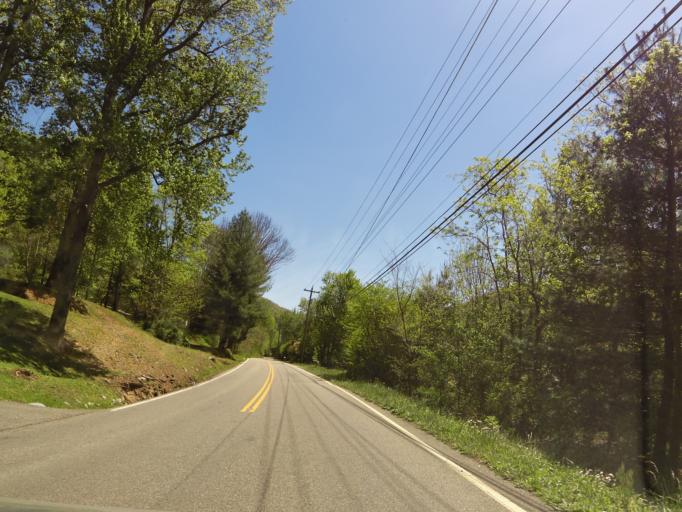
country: US
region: Tennessee
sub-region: Unicoi County
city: Erwin
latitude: 36.1658
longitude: -82.4435
